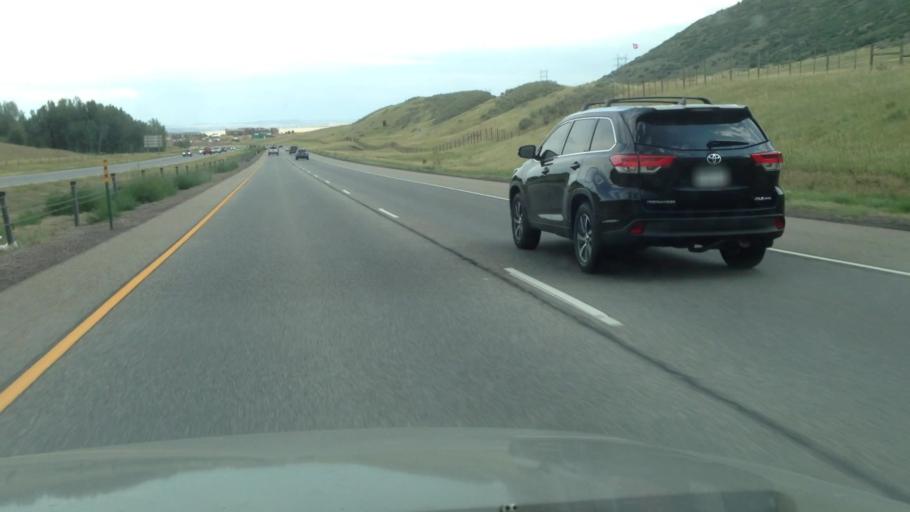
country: US
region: Colorado
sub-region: Jefferson County
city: Ken Caryl
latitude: 39.5690
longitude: -105.1336
